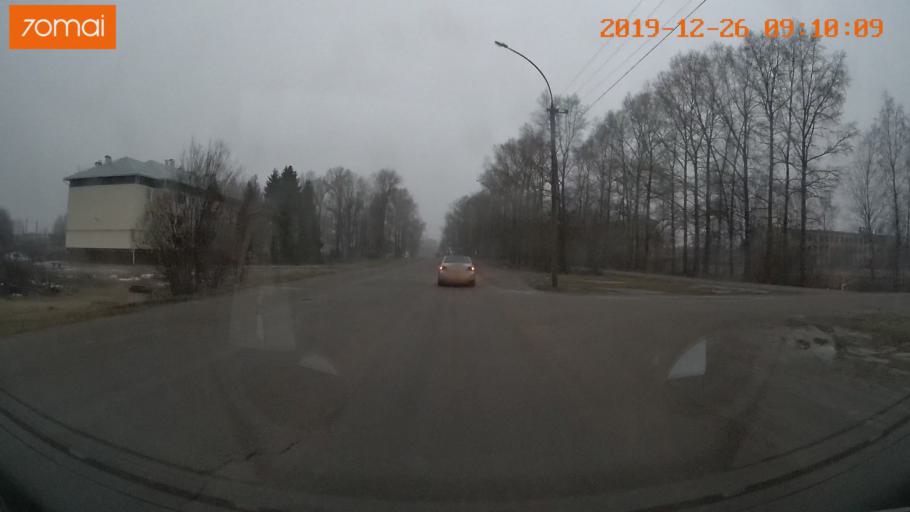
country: RU
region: Vologda
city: Gryazovets
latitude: 58.8692
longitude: 40.2528
